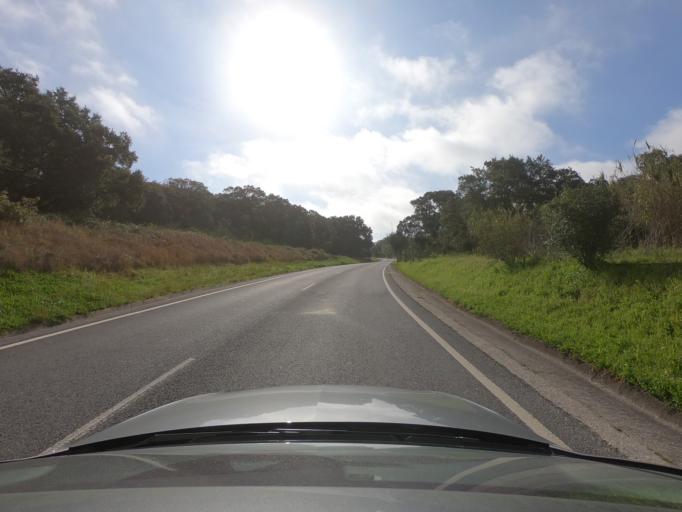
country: PT
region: Lisbon
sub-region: Oeiras
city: Barcarena
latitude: 38.7281
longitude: -9.2725
